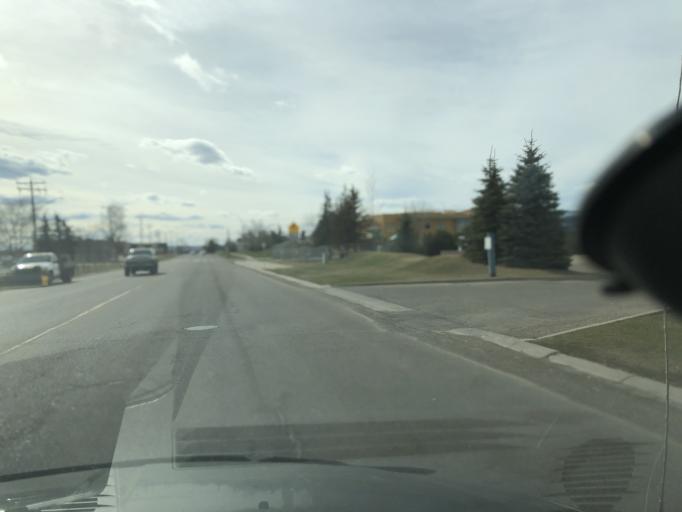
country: CA
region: Alberta
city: Calgary
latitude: 51.0689
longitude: -114.0072
